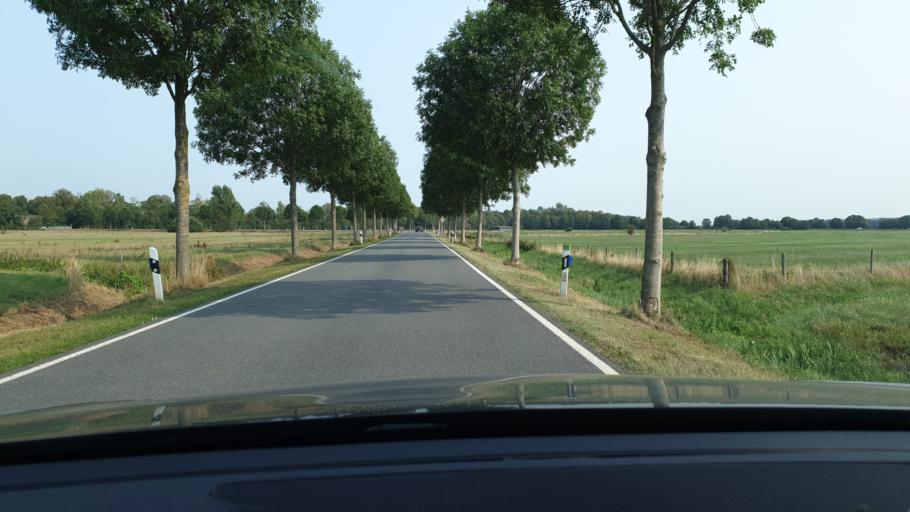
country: DE
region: North Rhine-Westphalia
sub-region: Regierungsbezirk Dusseldorf
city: Kranenburg
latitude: 51.7973
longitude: 6.0118
